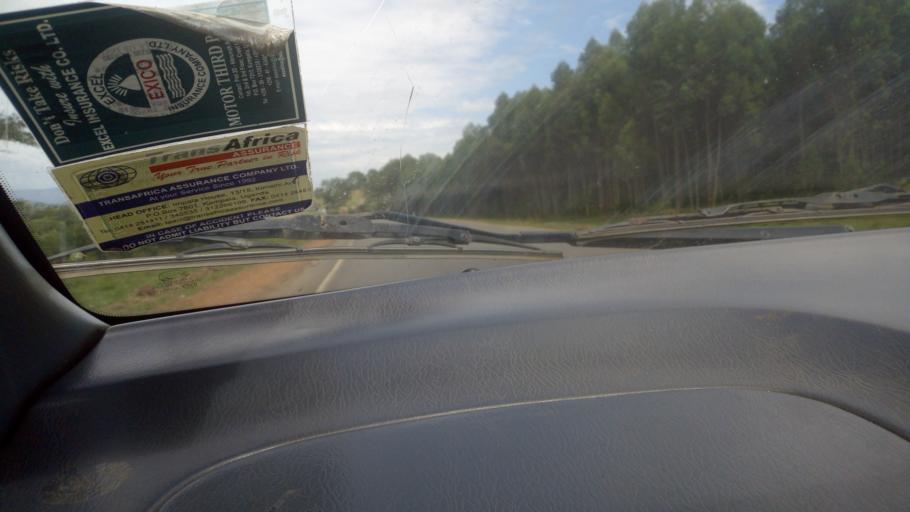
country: UG
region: Western Region
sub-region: Mbarara District
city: Bwizibwera
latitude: -0.3996
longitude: 30.5680
